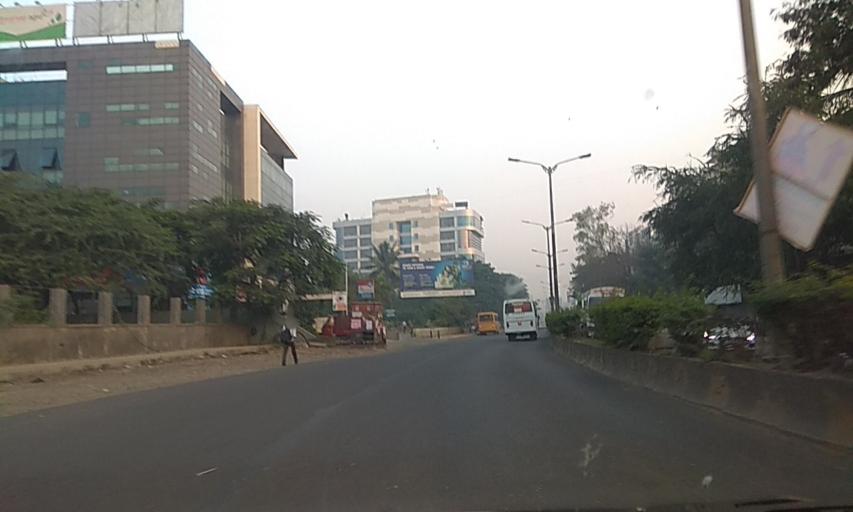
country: IN
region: Maharashtra
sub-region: Pune Division
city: Pune
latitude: 18.5215
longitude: 73.9321
